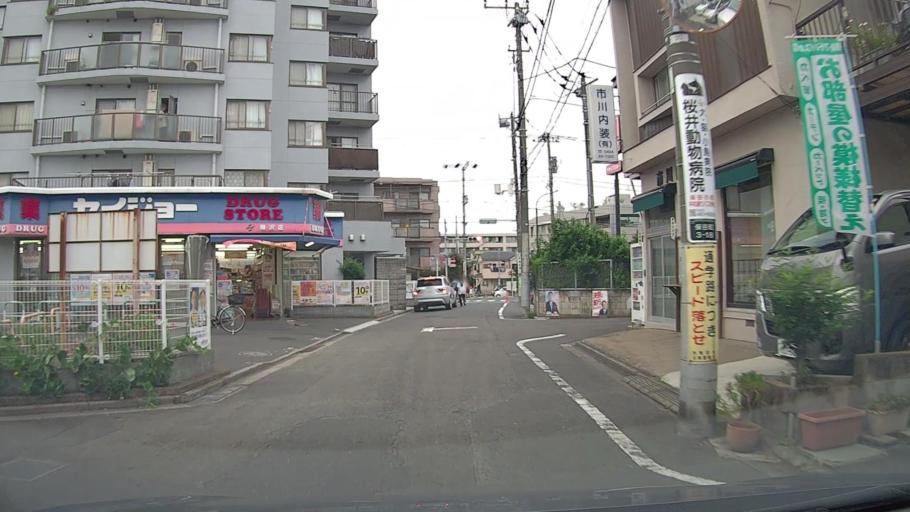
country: JP
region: Tokyo
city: Nishi-Tokyo-shi
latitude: 35.7313
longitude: 139.5504
